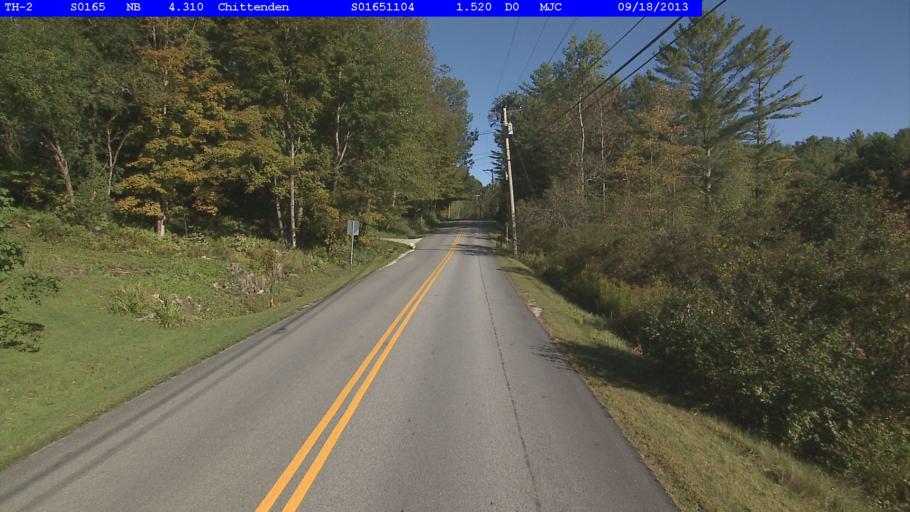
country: US
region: Vermont
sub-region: Rutland County
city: Rutland
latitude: 43.6977
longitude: -72.9580
